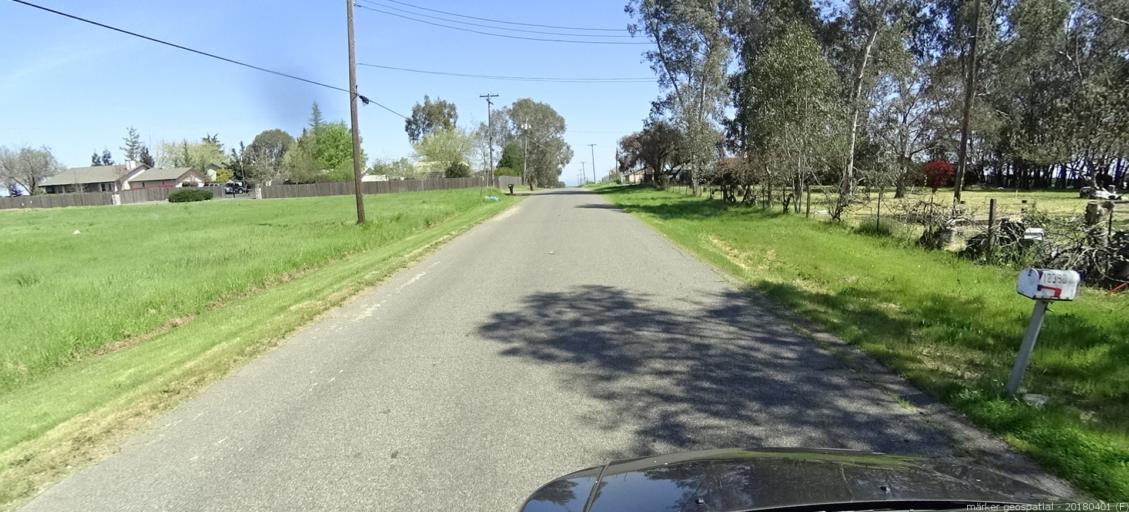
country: US
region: California
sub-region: Sacramento County
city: Wilton
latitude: 38.3941
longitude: -121.2109
